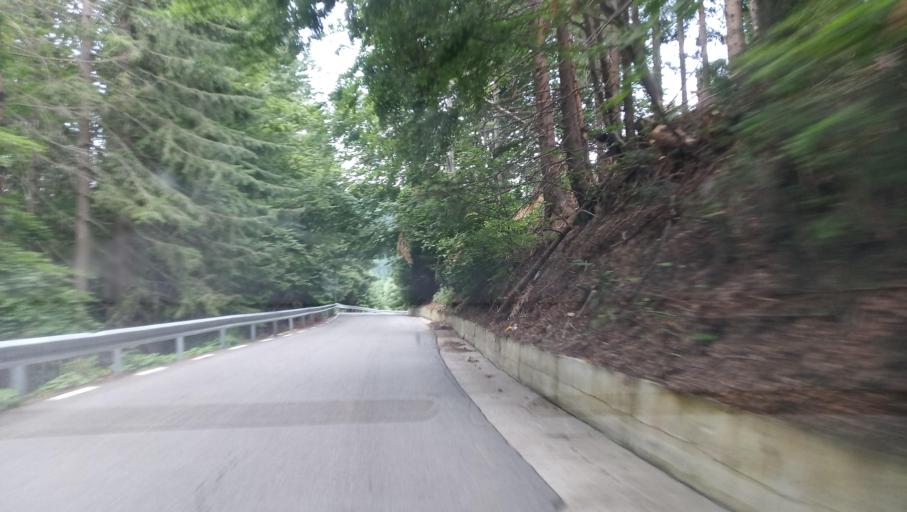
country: RO
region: Prahova
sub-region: Oras Sinaia
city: Sinaia
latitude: 45.3210
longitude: 25.4876
